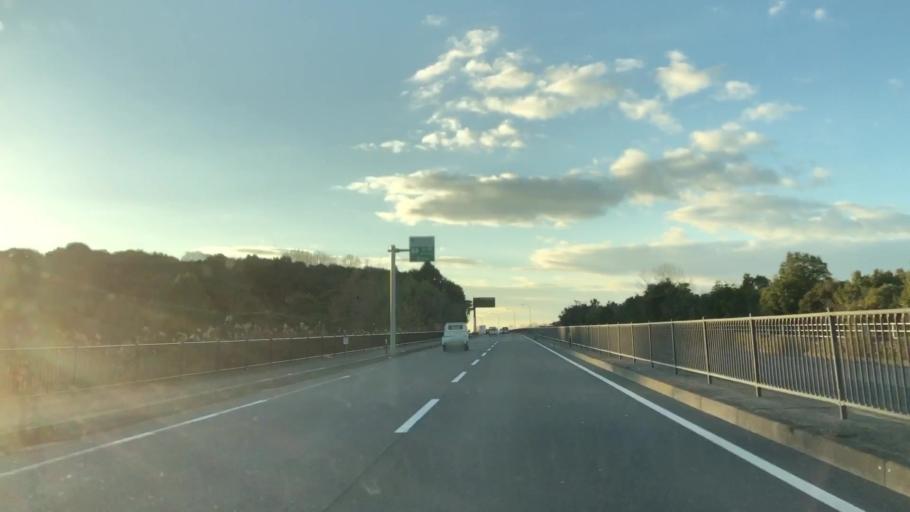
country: JP
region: Fukuoka
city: Nakatsu
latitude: 33.5538
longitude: 131.2565
